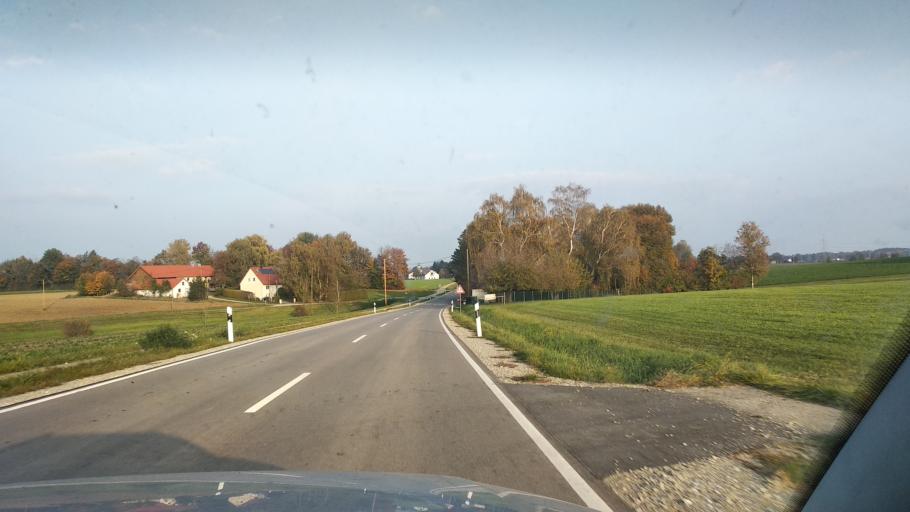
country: DE
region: Bavaria
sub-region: Upper Bavaria
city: Worth
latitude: 48.2412
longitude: 11.9216
